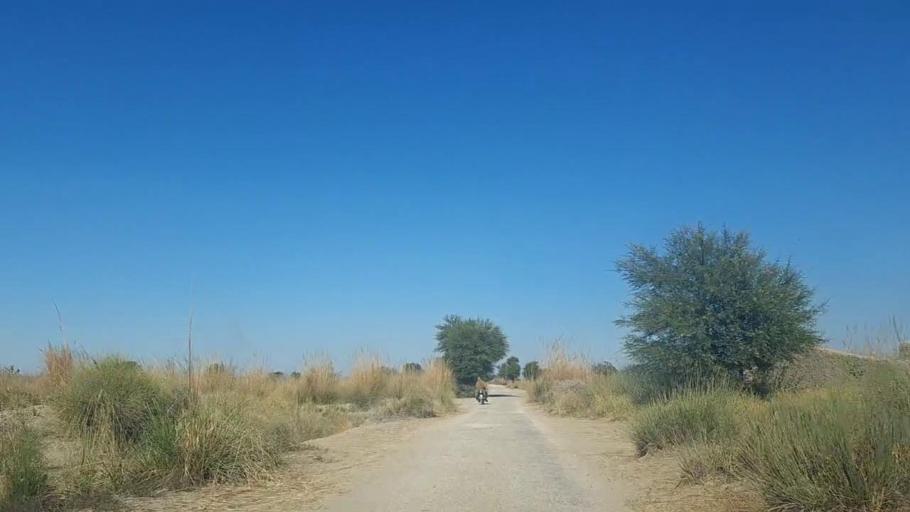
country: PK
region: Sindh
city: Khadro
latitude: 26.2146
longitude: 68.8602
